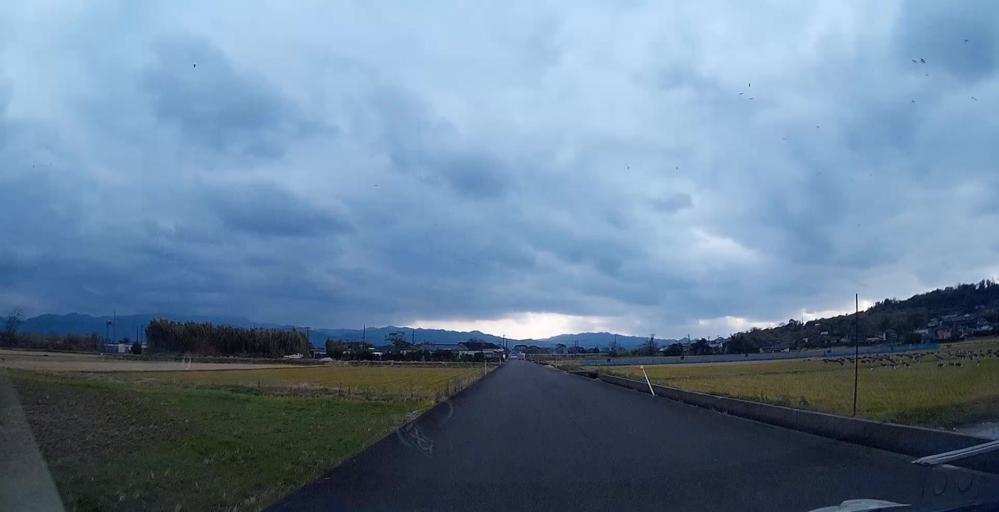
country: JP
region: Kagoshima
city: Izumi
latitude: 32.0980
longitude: 130.2754
